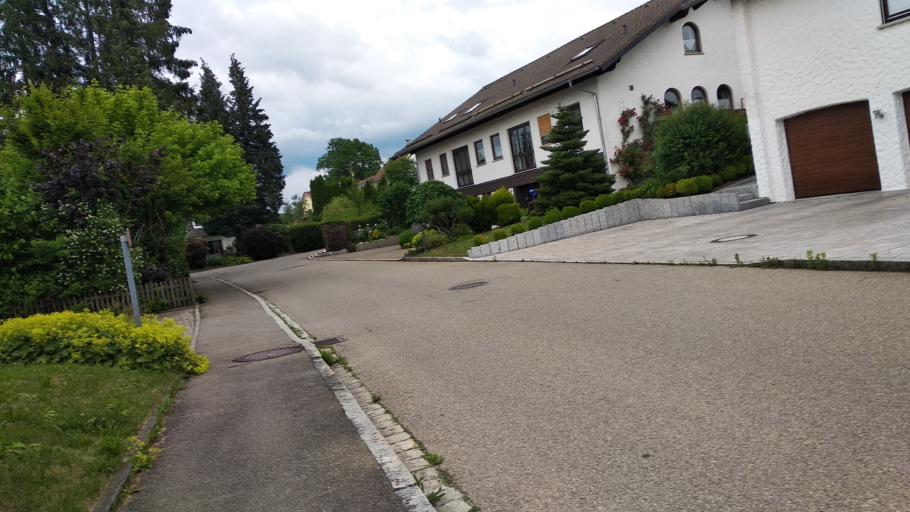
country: DE
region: Baden-Wuerttemberg
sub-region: Tuebingen Region
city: Aichstetten
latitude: 47.8890
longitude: 10.0745
